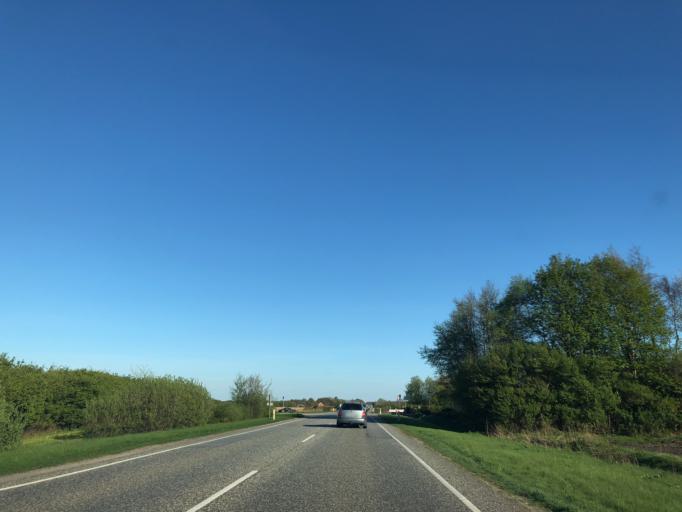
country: DK
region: Central Jutland
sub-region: Holstebro Kommune
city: Holstebro
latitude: 56.3077
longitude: 8.7015
